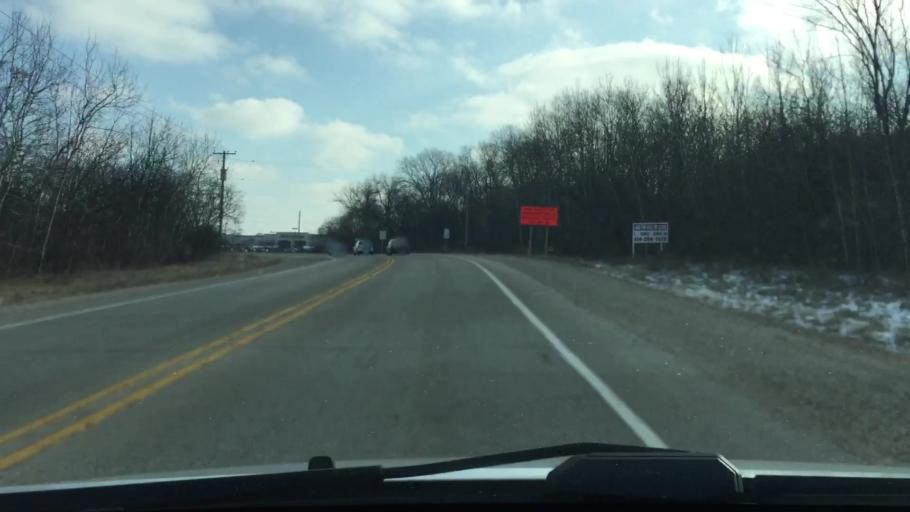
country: US
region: Wisconsin
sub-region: Waukesha County
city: Wales
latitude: 43.0109
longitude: -88.3905
